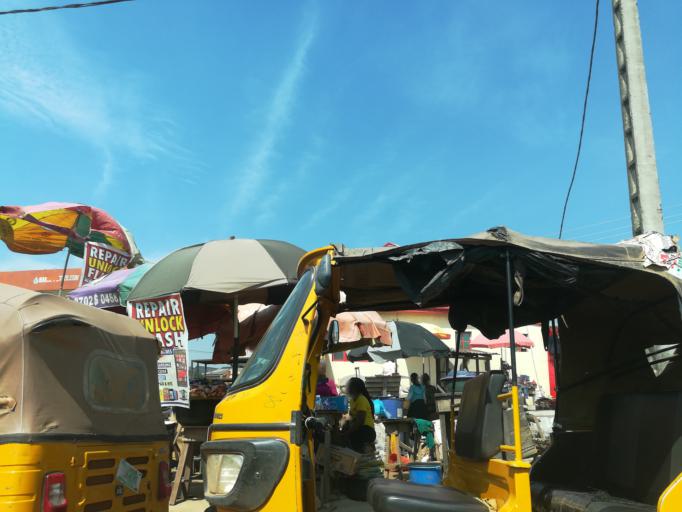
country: NG
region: Lagos
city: Ikorodu
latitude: 6.6276
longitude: 3.4837
